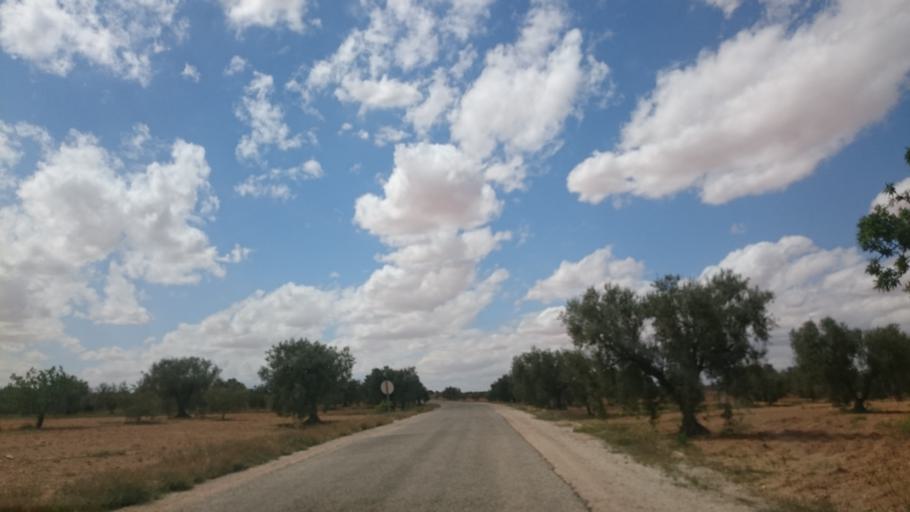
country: TN
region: Safaqis
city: Bi'r `Ali Bin Khalifah
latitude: 34.7771
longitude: 10.3615
